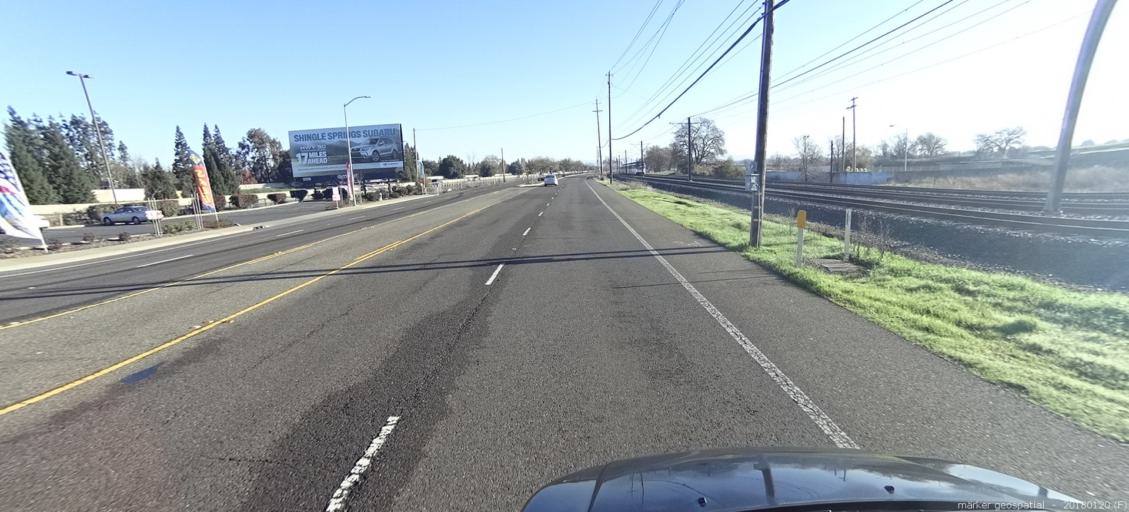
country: US
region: California
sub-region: Sacramento County
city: Gold River
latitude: 38.6169
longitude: -121.2476
